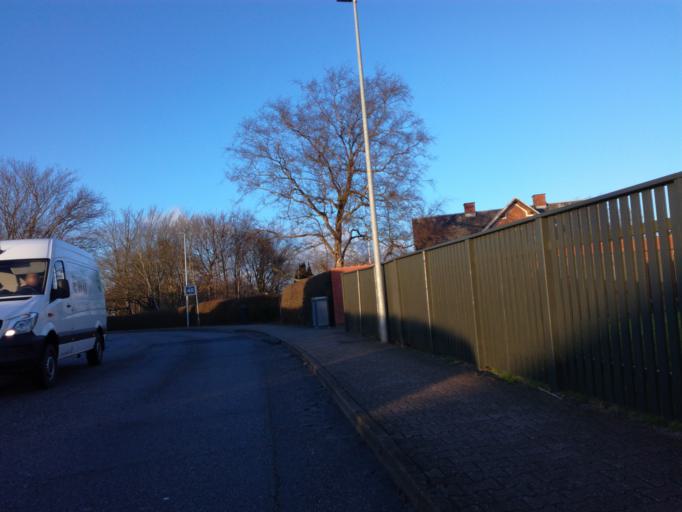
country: DK
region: South Denmark
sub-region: Fredericia Kommune
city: Taulov
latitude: 55.5382
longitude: 9.6094
